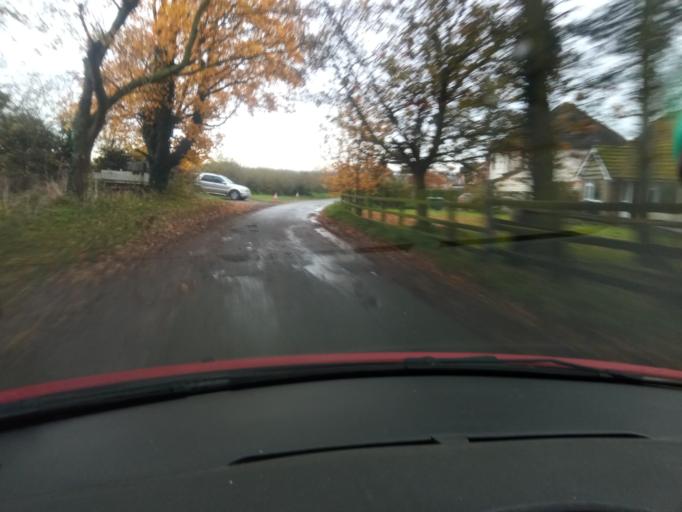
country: GB
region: England
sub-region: Derbyshire
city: Borrowash
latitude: 52.8633
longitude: -1.3945
